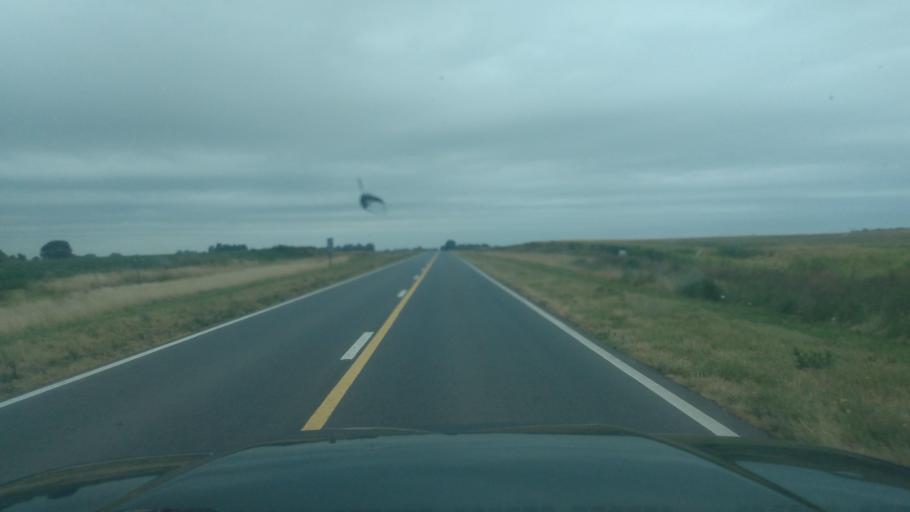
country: AR
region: Buenos Aires
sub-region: Partido de Bragado
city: Bragado
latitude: -35.3139
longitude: -60.6299
